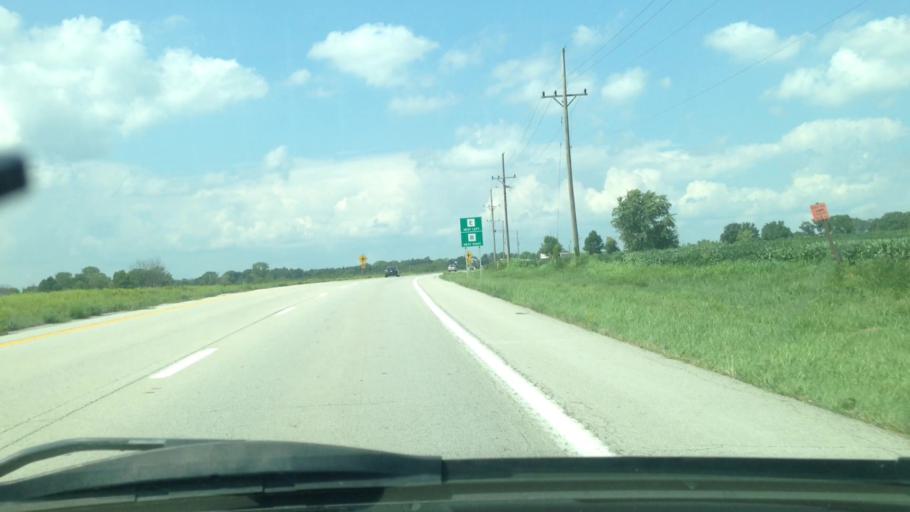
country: US
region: Missouri
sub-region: Lincoln County
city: Troy
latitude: 39.1230
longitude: -90.9626
